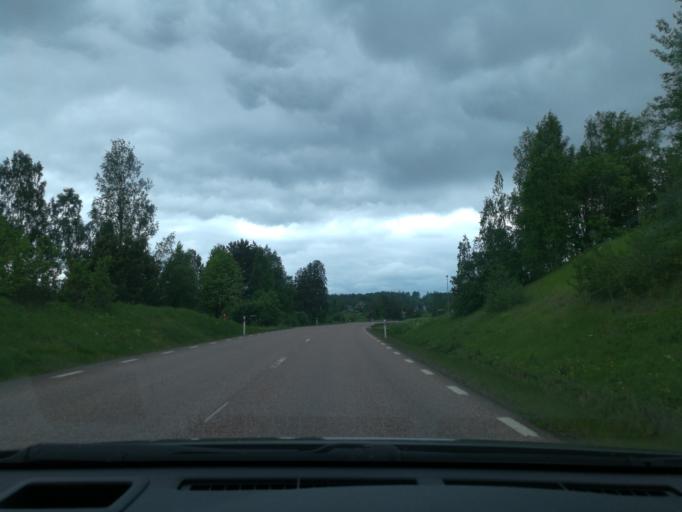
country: SE
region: Dalarna
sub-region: Smedjebackens Kommun
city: Smedjebacken
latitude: 60.1292
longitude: 15.4244
